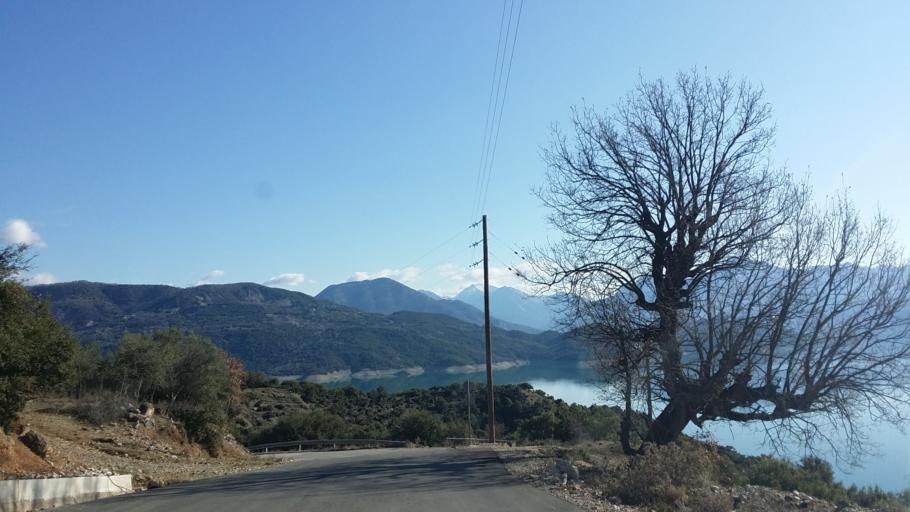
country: GR
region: Central Greece
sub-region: Nomos Evrytanias
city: Kerasochori
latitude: 38.9653
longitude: 21.4805
